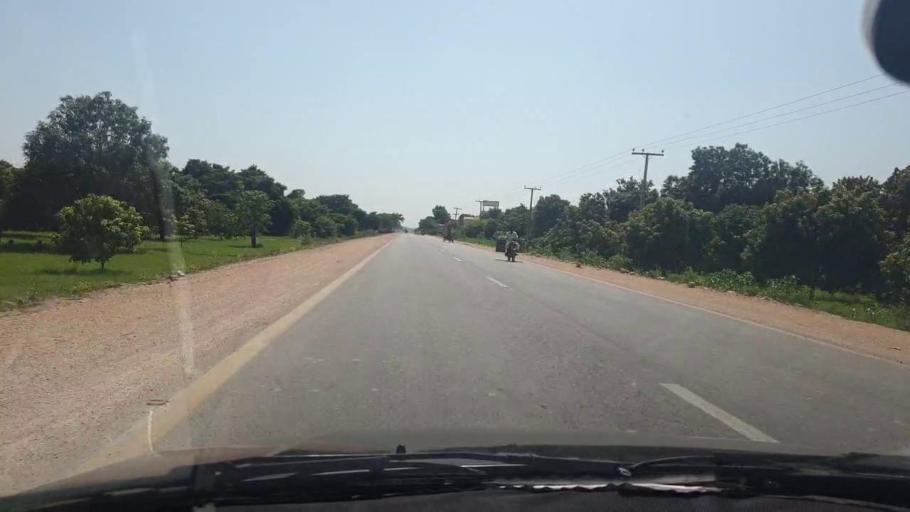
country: PK
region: Sindh
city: Chambar
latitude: 25.3233
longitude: 68.8013
